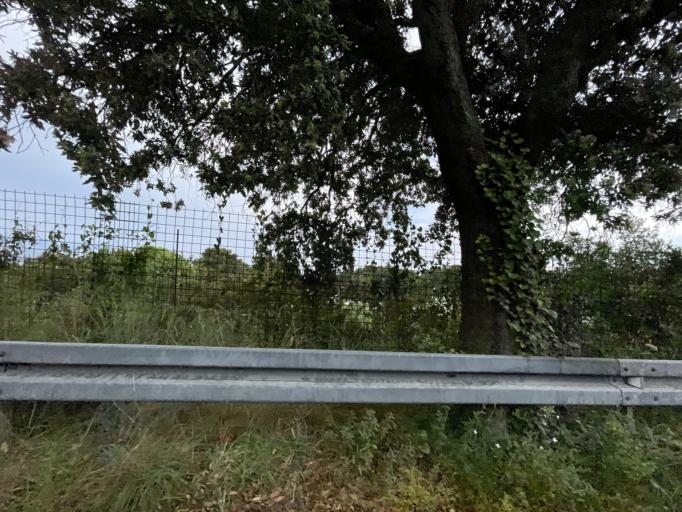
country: HR
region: Splitsko-Dalmatinska
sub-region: Grad Split
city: Split
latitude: 43.5052
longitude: 16.4041
